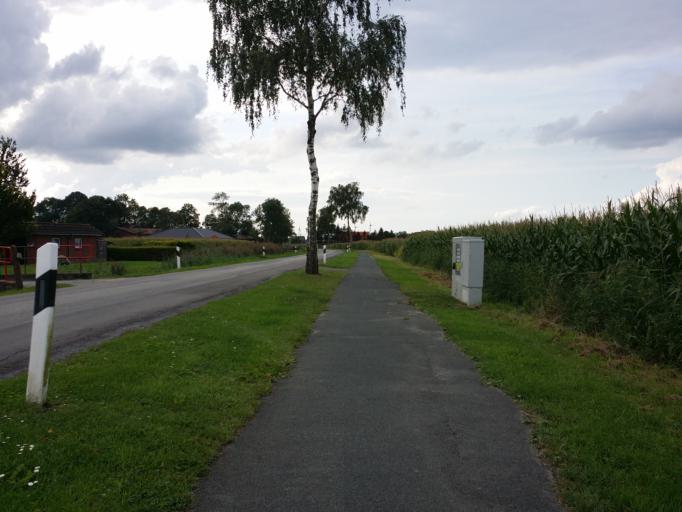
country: DE
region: Lower Saxony
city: Oederquart
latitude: 53.7845
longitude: 9.2387
